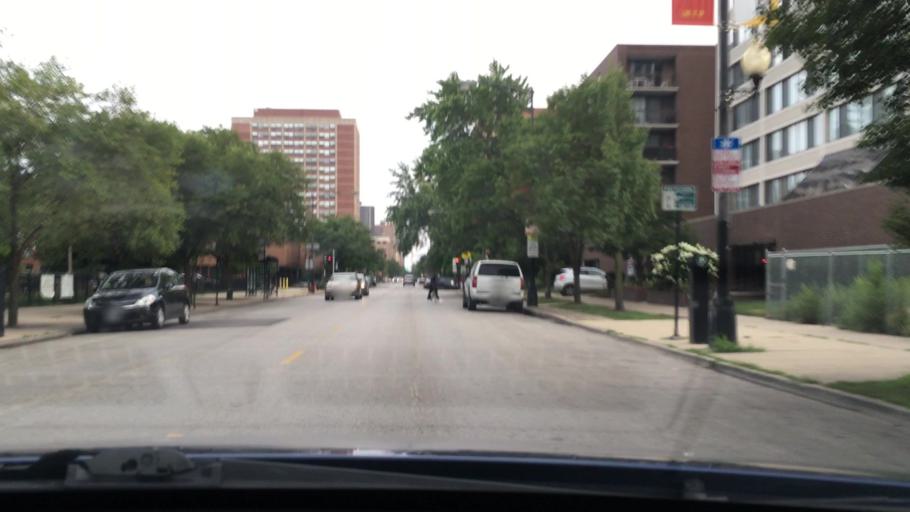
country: US
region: Illinois
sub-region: Cook County
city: Evanston
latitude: 41.9724
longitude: -87.6550
